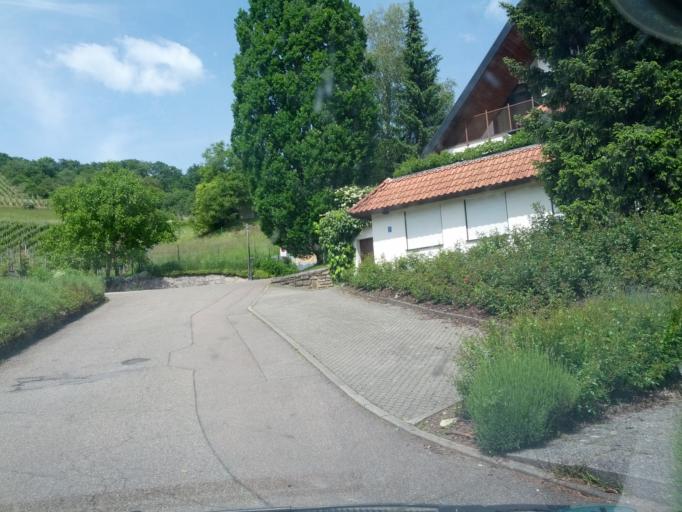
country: DE
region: Baden-Wuerttemberg
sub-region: Freiburg Region
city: Ebringen
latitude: 47.9587
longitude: 7.7850
